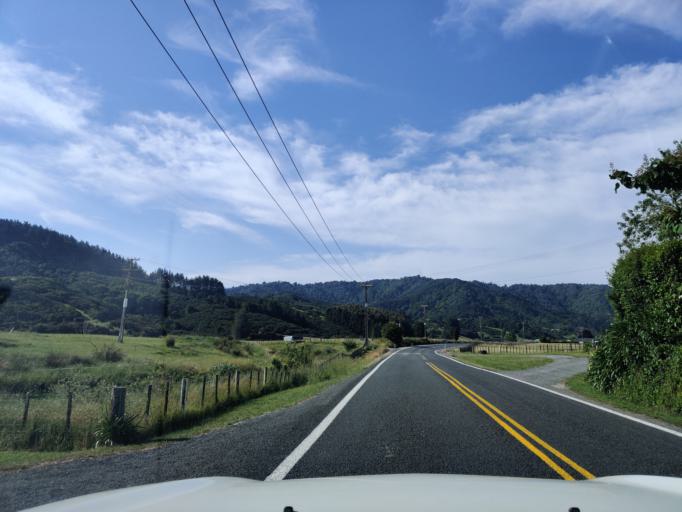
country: NZ
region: Waikato
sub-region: Waikato District
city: Ngaruawahia
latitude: -37.6470
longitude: 175.1453
